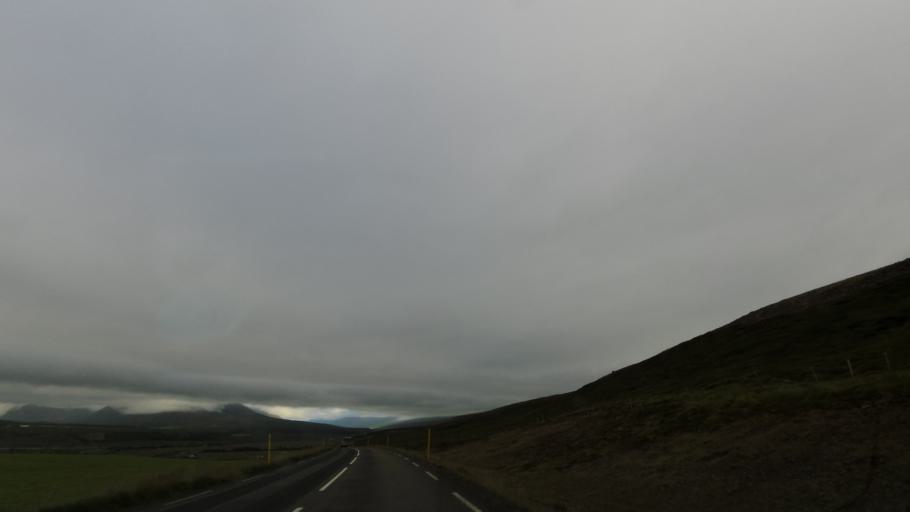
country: IS
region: Northeast
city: Akureyri
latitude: 65.7811
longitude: -17.9227
